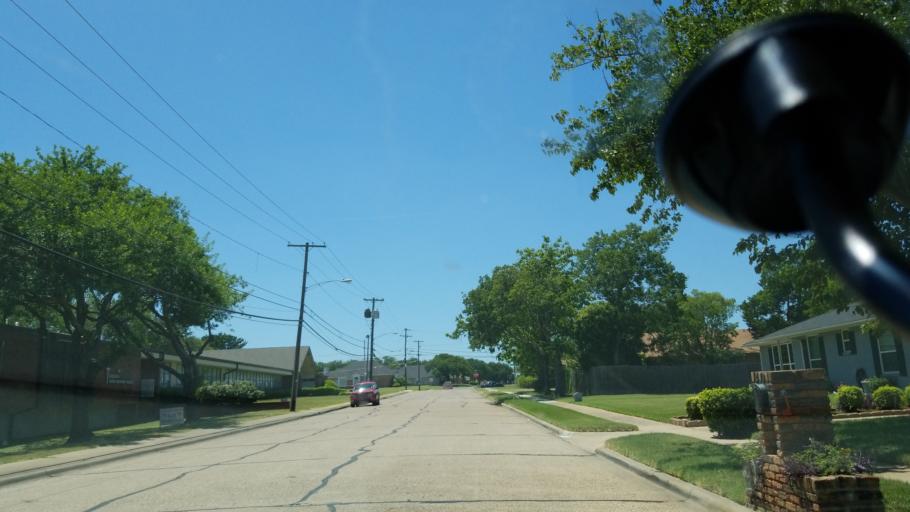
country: US
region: Texas
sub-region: Dallas County
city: Cockrell Hill
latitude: 32.6882
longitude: -96.8384
